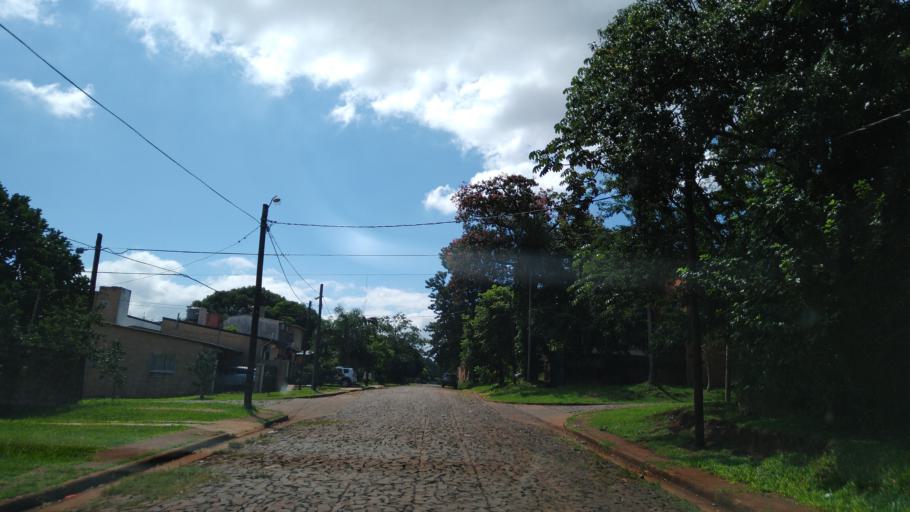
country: AR
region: Misiones
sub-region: Departamento de Capital
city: Posadas
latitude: -27.3988
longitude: -55.9146
